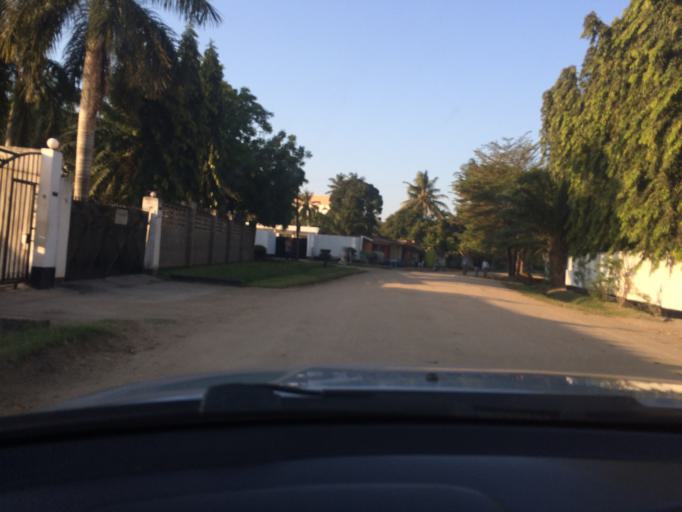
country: TZ
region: Dar es Salaam
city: Magomeni
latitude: -6.7757
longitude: 39.2552
